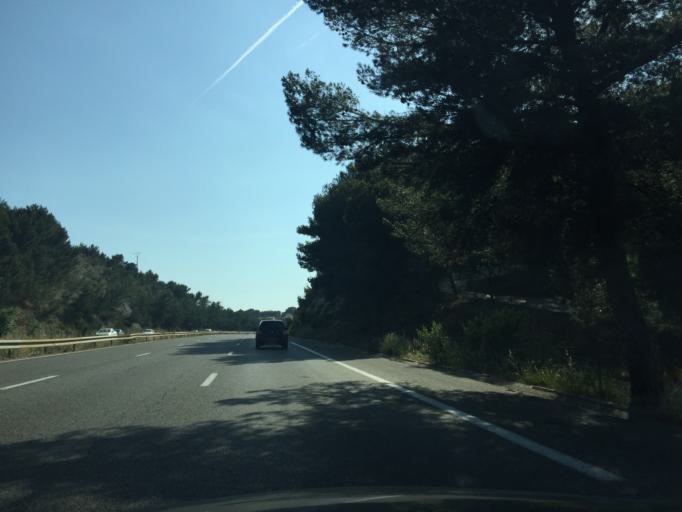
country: FR
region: Provence-Alpes-Cote d'Azur
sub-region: Departement des Bouches-du-Rhone
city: Martigues
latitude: 43.3958
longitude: 5.0682
